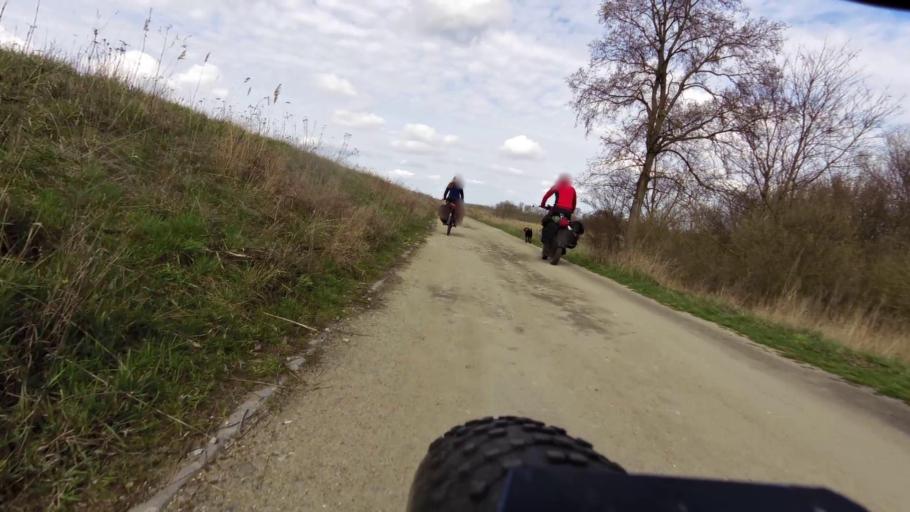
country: DE
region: Brandenburg
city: Lebus
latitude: 52.4252
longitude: 14.5477
